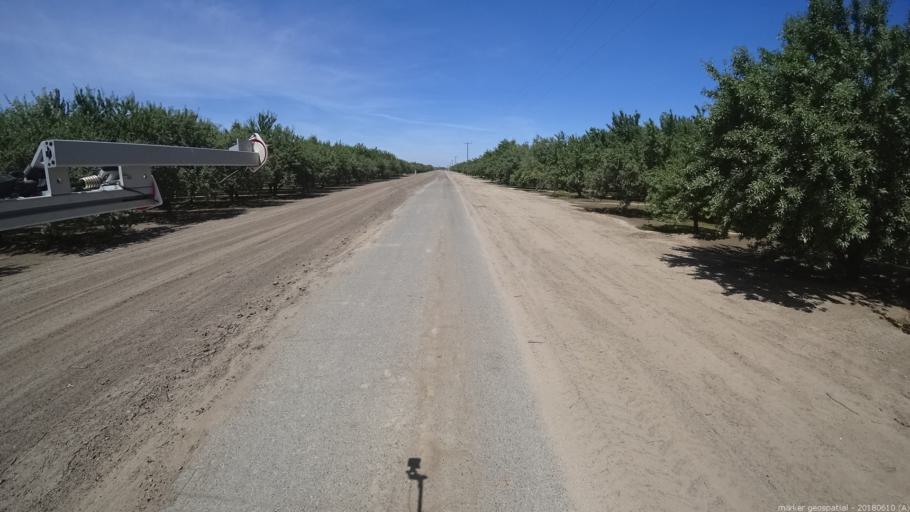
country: US
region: California
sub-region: Madera County
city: Chowchilla
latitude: 37.0471
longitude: -120.3884
